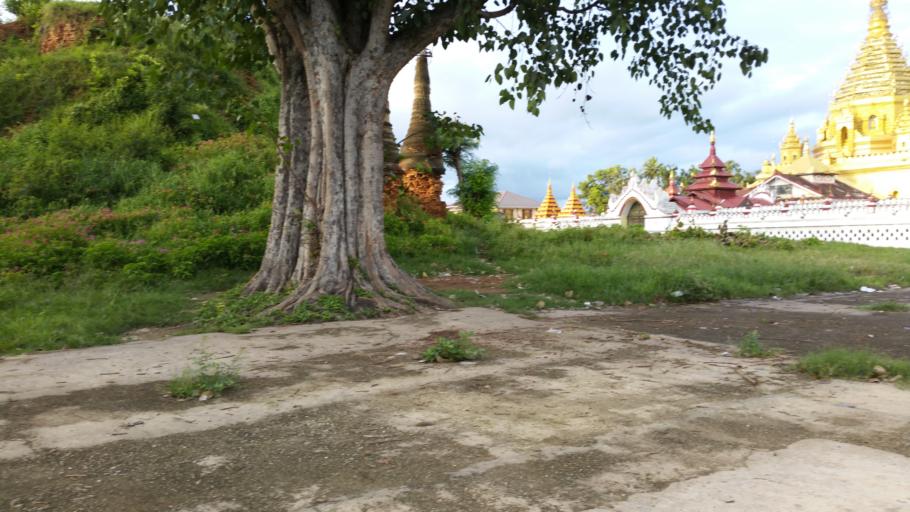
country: MM
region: Shan
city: Taunggyi
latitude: 20.6585
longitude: 96.9299
